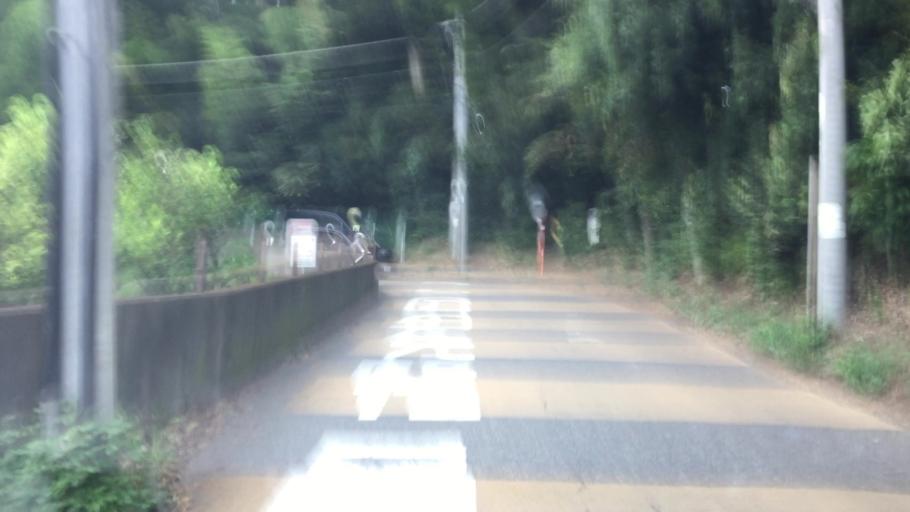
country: JP
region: Chiba
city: Matsudo
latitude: 35.8001
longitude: 139.9360
